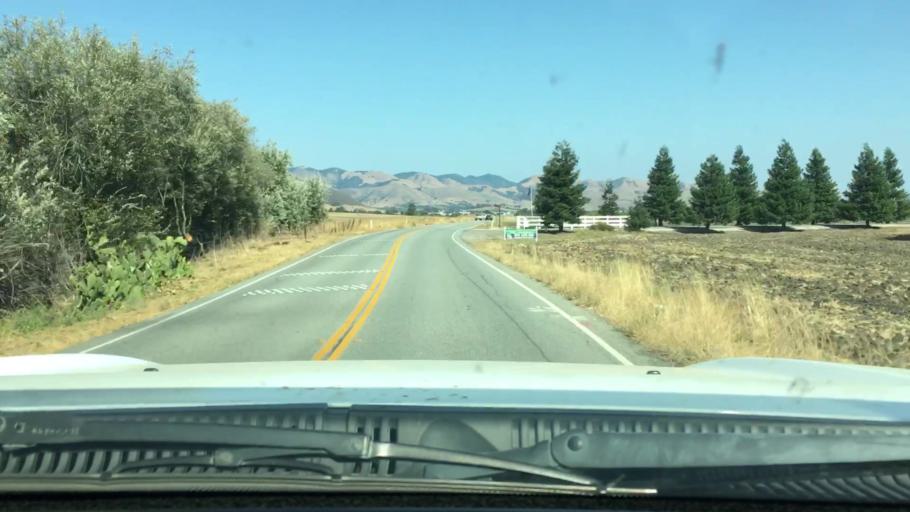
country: US
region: California
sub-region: San Luis Obispo County
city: San Luis Obispo
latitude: 35.2359
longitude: -120.6729
